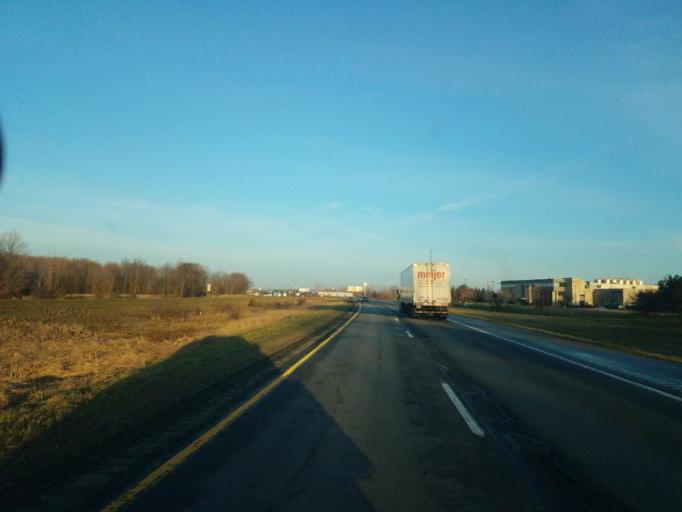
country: US
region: Michigan
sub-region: Livingston County
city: Fowlerville
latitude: 42.6466
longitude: -84.0526
